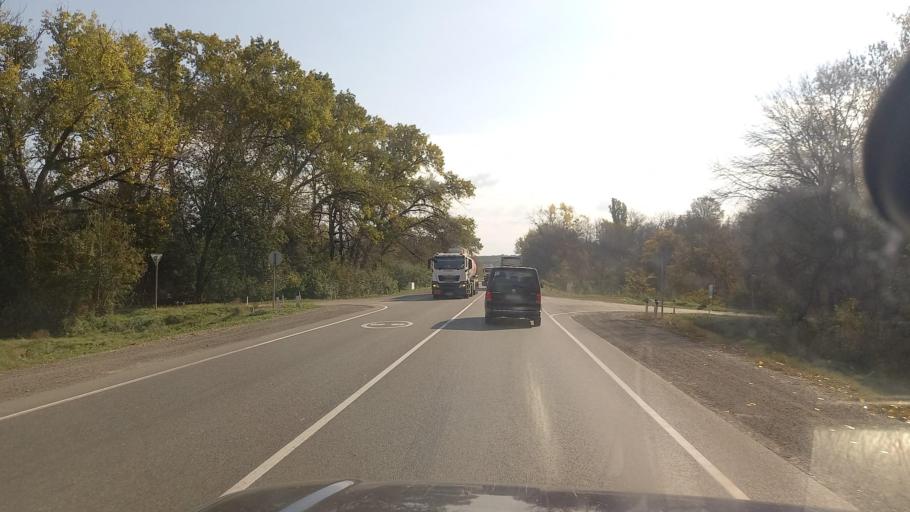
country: RU
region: Krasnodarskiy
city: Abinsk
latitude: 44.8434
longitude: 38.1560
